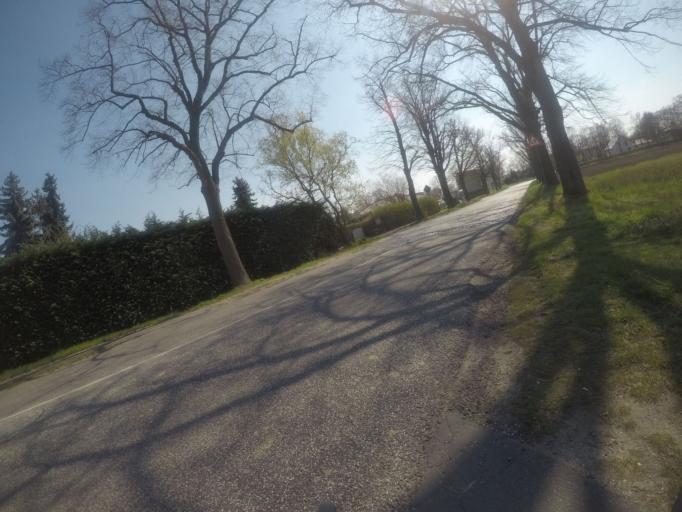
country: DE
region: Brandenburg
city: Nauen
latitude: 52.5817
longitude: 12.8748
